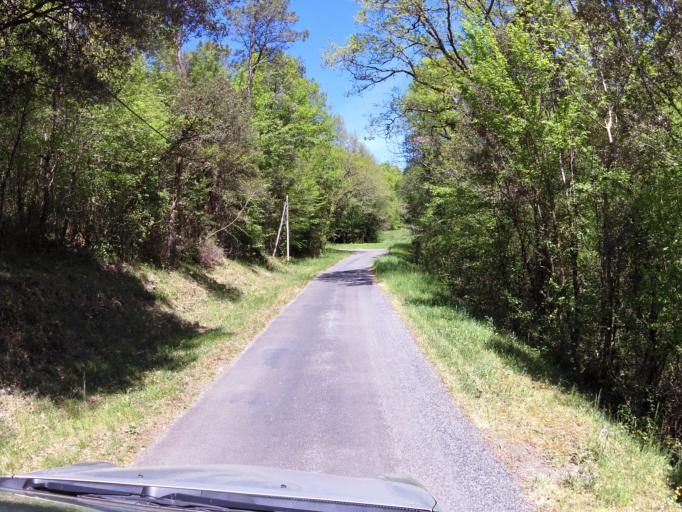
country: FR
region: Aquitaine
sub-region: Departement de la Dordogne
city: Sarlat-la-Caneda
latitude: 44.9263
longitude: 1.1474
